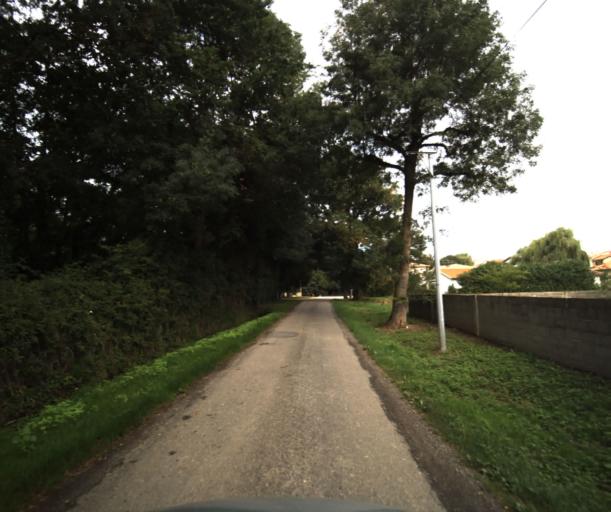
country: FR
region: Midi-Pyrenees
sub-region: Departement de la Haute-Garonne
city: Le Fauga
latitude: 43.4412
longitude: 1.2945
